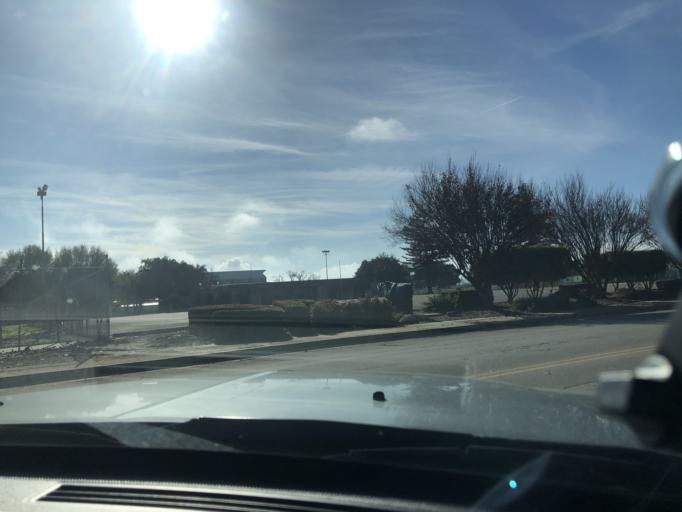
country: US
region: California
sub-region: Monterey County
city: King City
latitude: 36.2064
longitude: -121.1282
